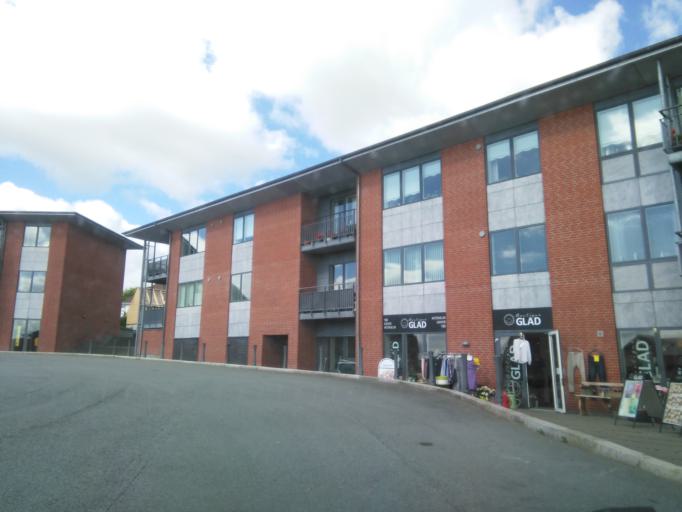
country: DK
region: Central Jutland
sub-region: Syddjurs Kommune
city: Ronde
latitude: 56.3005
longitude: 10.4788
